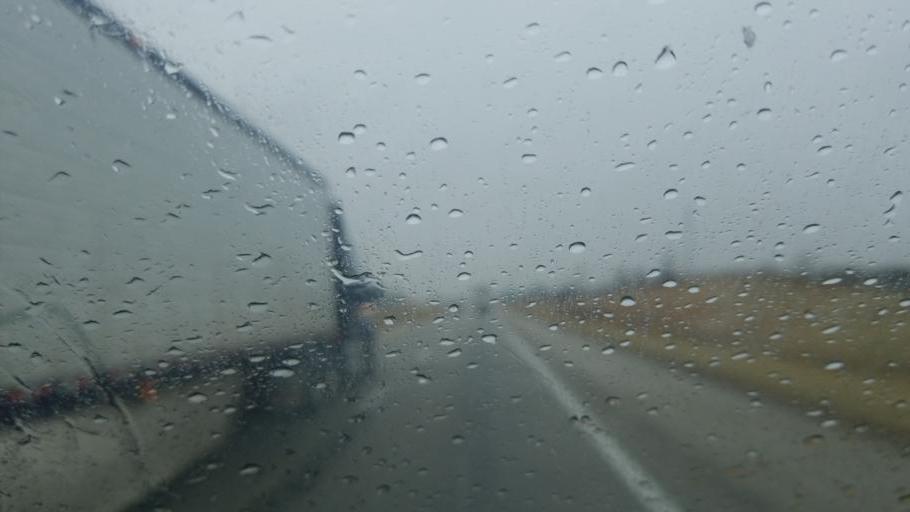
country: US
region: Ohio
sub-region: Preble County
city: Lewisburg
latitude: 39.8358
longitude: -84.6169
